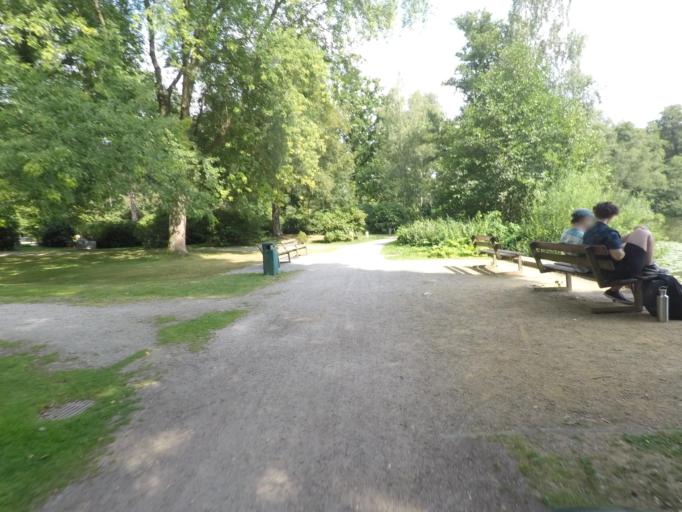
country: DE
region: Hamburg
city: Wellingsbuettel
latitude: 53.6289
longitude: 10.0669
